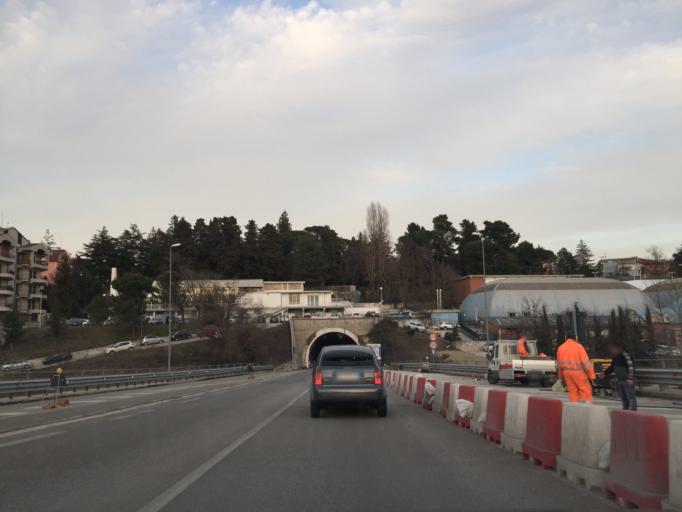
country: IT
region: Molise
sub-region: Provincia di Campobasso
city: Campobasso
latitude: 41.5545
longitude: 14.6540
